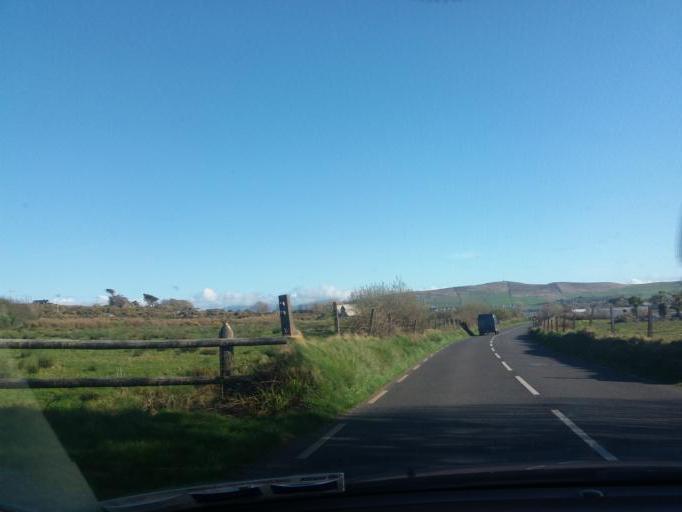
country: IE
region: Munster
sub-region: Ciarrai
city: Dingle
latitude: 52.1472
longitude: -10.2892
